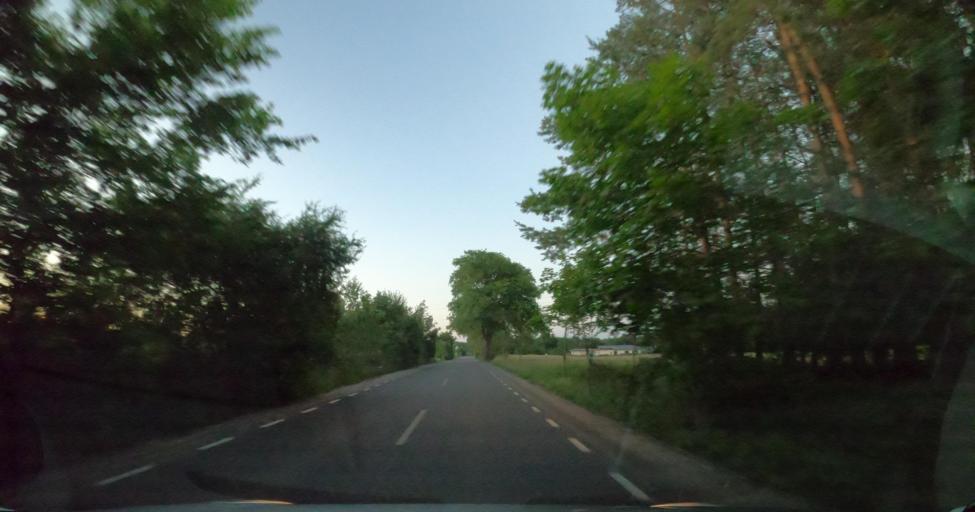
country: PL
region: Pomeranian Voivodeship
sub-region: Powiat wejherowski
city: Szemud
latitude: 54.4727
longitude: 18.1727
